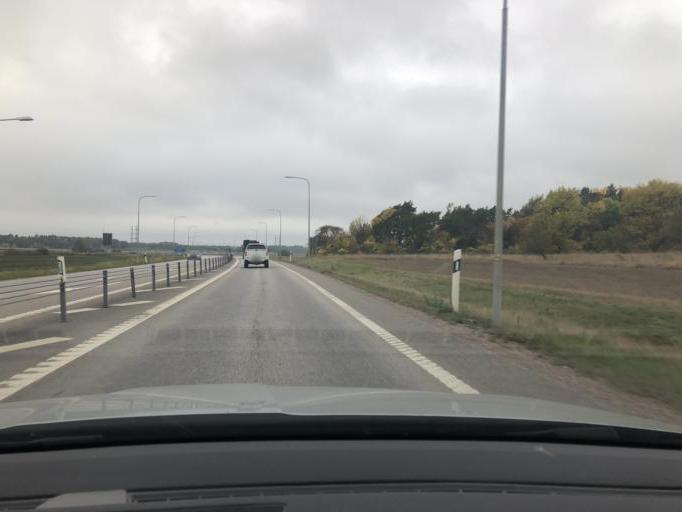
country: SE
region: Uppsala
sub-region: Uppsala Kommun
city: Gamla Uppsala
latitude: 59.8897
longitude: 17.6826
